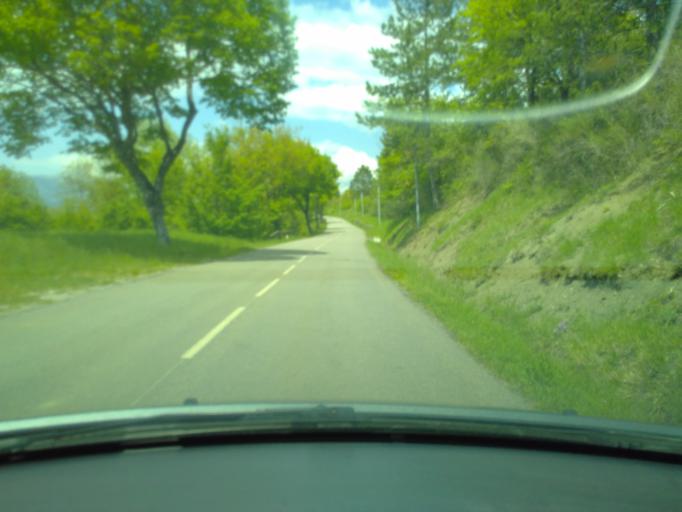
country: FR
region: Rhone-Alpes
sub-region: Departement de la Drome
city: Die
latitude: 44.6258
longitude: 5.4428
